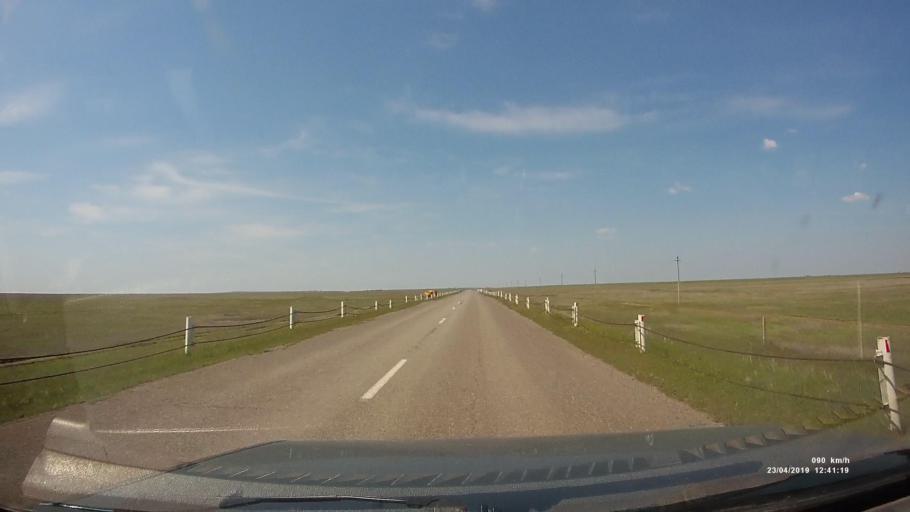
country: RU
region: Kalmykiya
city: Yashalta
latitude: 46.4475
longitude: 42.6824
